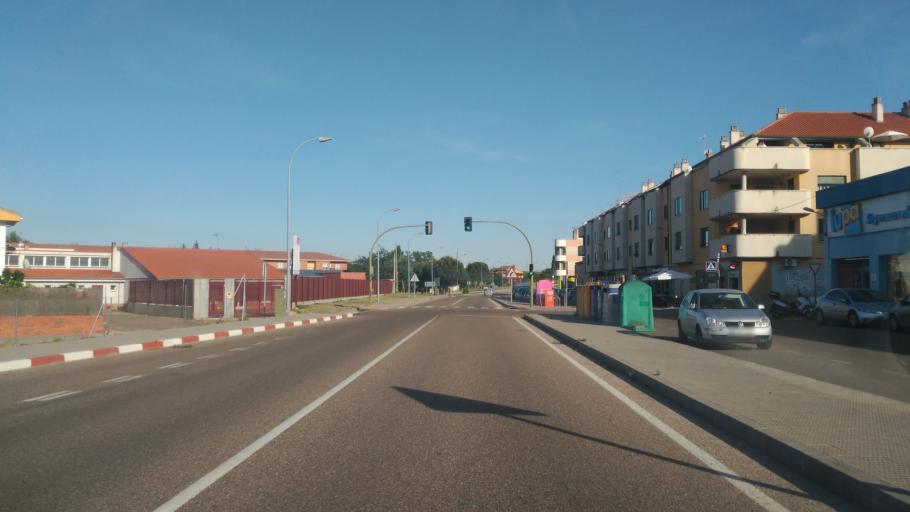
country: ES
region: Castille and Leon
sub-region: Provincia de Zamora
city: Morales del Vino
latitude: 41.4441
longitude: -5.7332
